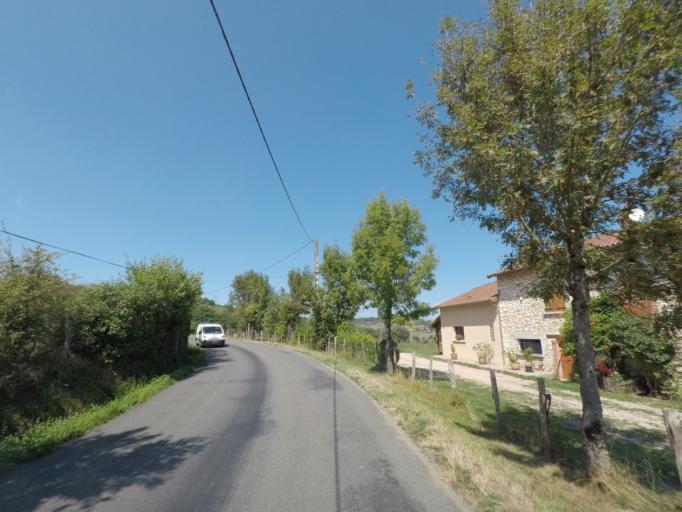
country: FR
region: Midi-Pyrenees
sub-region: Departement de l'Aveyron
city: Livinhac-le-Haut
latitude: 44.6137
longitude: 2.2158
